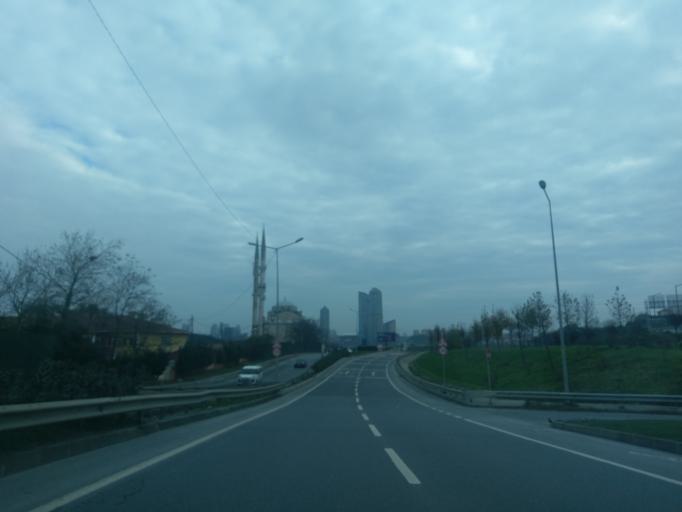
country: TR
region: Istanbul
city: Sisli
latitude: 41.1006
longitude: 28.9601
